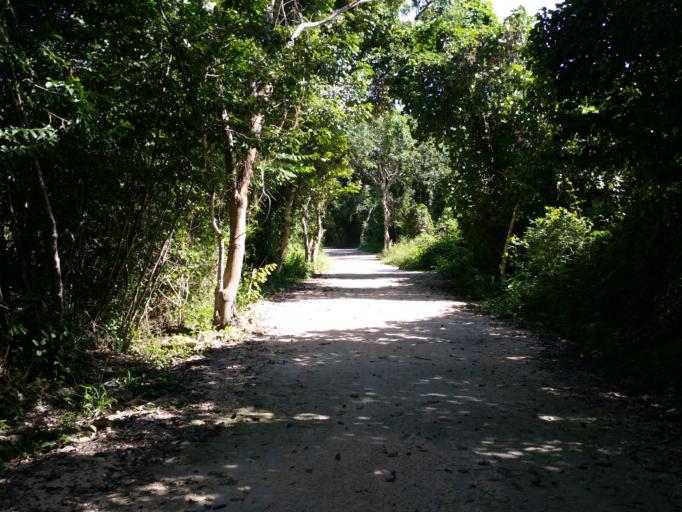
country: MX
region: Yucatan
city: Temozon
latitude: 20.8890
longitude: -88.1305
